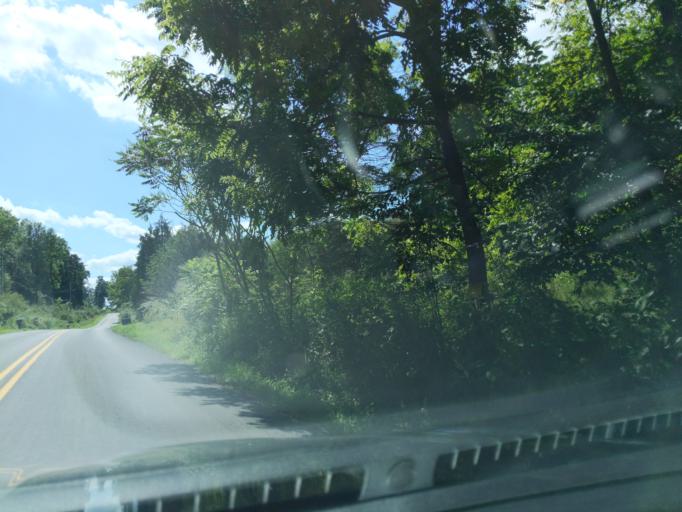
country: US
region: Pennsylvania
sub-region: Blair County
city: Tyrone
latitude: 40.6498
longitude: -78.2129
